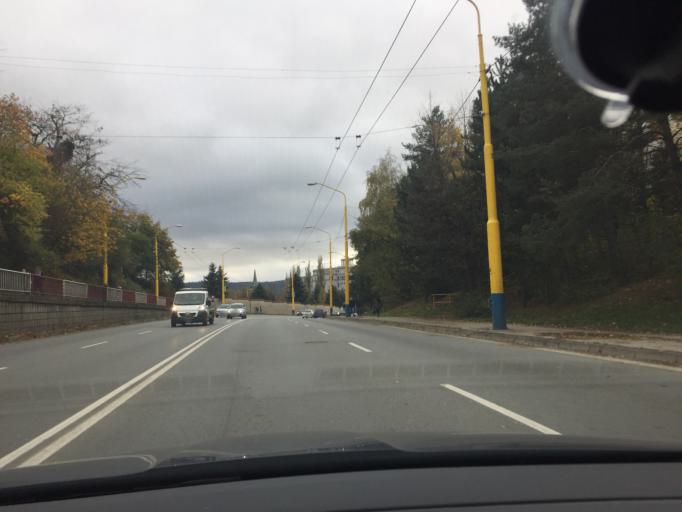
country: SK
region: Presovsky
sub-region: Okres Presov
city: Presov
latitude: 49.0042
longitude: 21.2442
